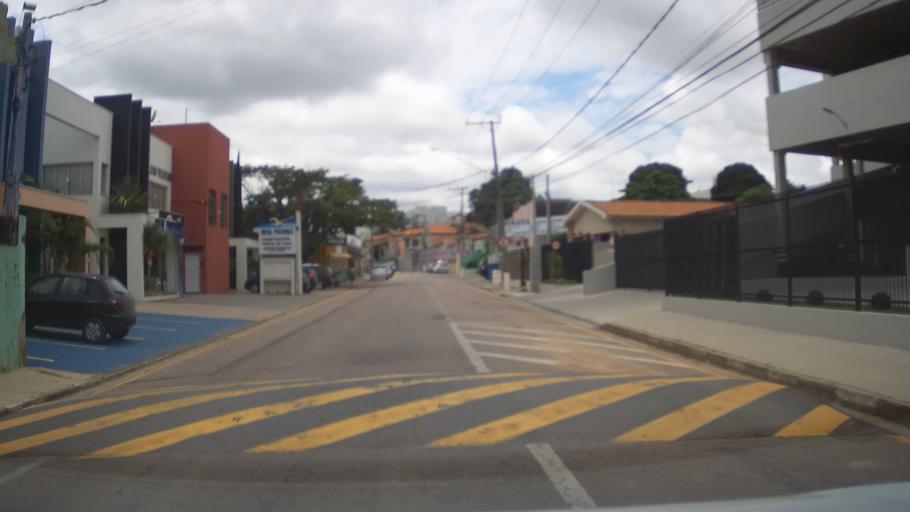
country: BR
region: Sao Paulo
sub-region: Vinhedo
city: Vinhedo
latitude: -23.0309
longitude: -46.9786
